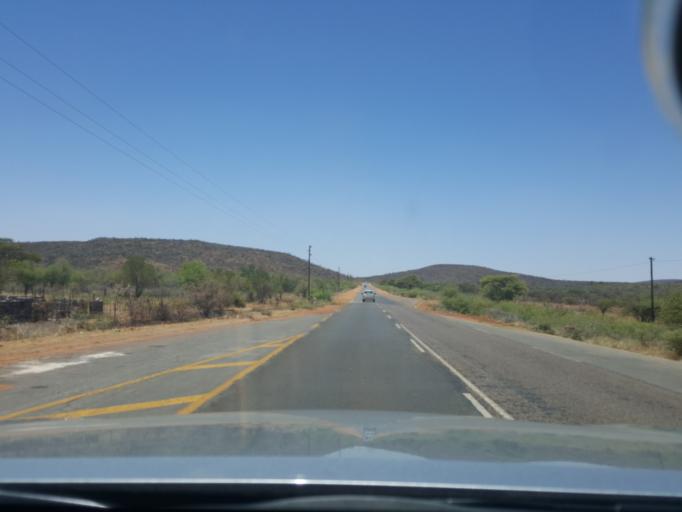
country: ZA
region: North-West
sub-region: Ngaka Modiri Molema District Municipality
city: Zeerust
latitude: -25.3712
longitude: 25.9354
